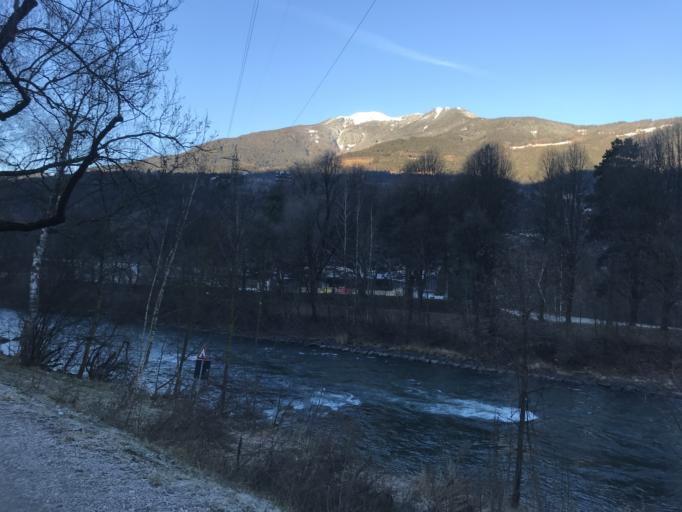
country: IT
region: Trentino-Alto Adige
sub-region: Bolzano
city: Bressanone
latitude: 46.7058
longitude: 11.6562
